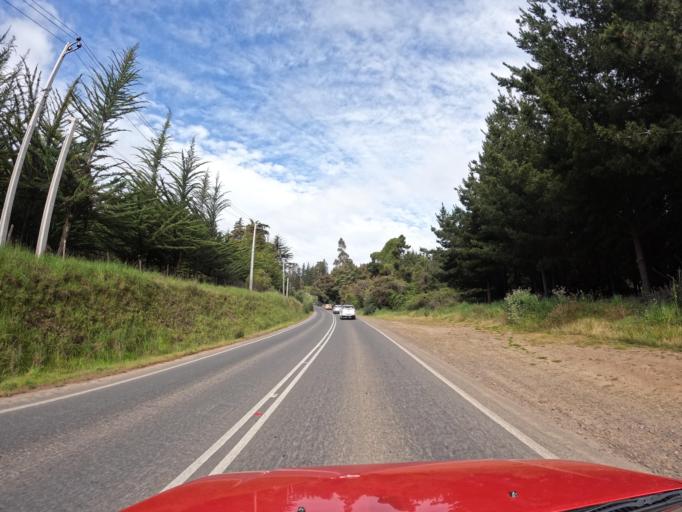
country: CL
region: O'Higgins
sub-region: Provincia de Colchagua
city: Santa Cruz
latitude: -34.3553
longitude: -71.9186
